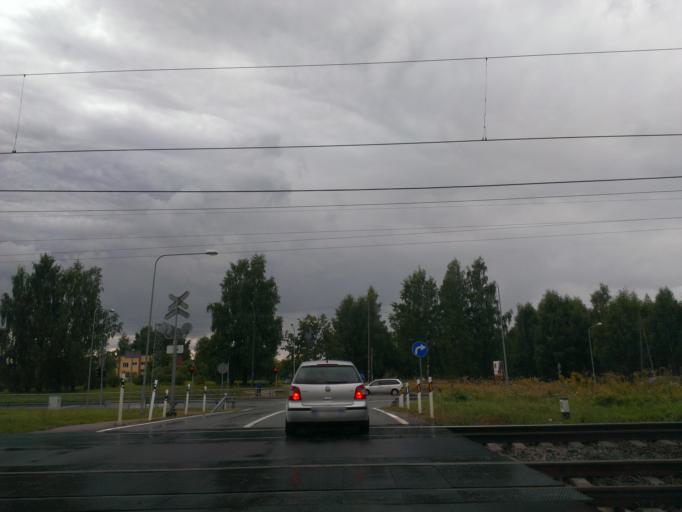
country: LV
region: Kegums
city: Kegums
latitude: 56.7479
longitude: 24.7180
